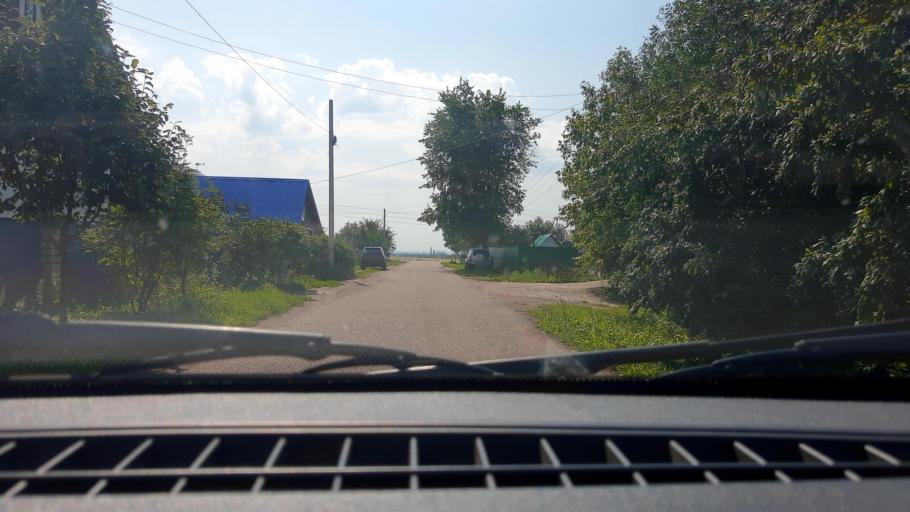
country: RU
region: Bashkortostan
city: Mikhaylovka
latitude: 54.8398
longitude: 55.8295
